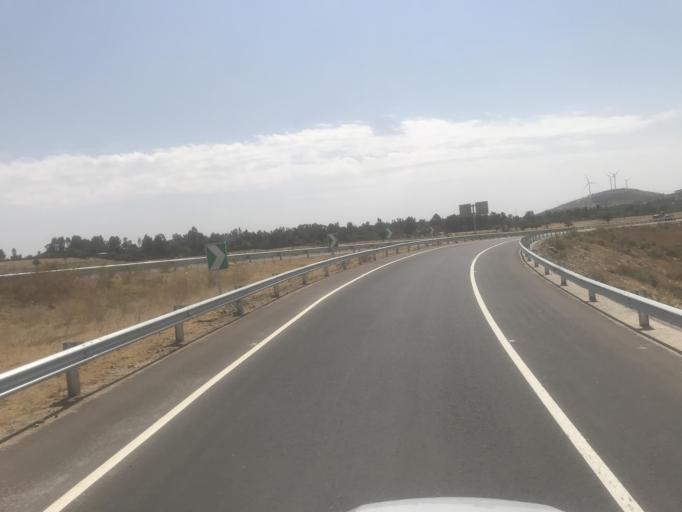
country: ET
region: Oromiya
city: Mojo
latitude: 8.5791
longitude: 39.1723
